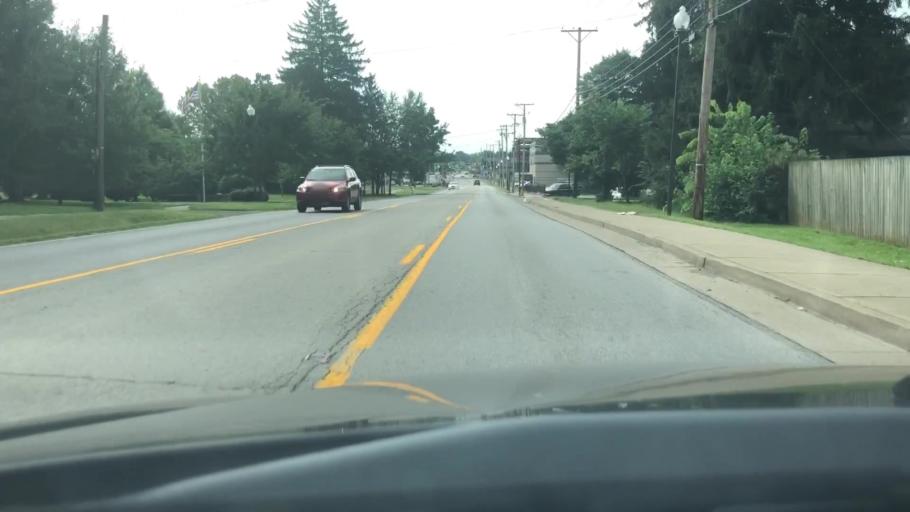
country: US
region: Kentucky
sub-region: Jefferson County
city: Lyndon
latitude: 38.2645
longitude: -85.6092
